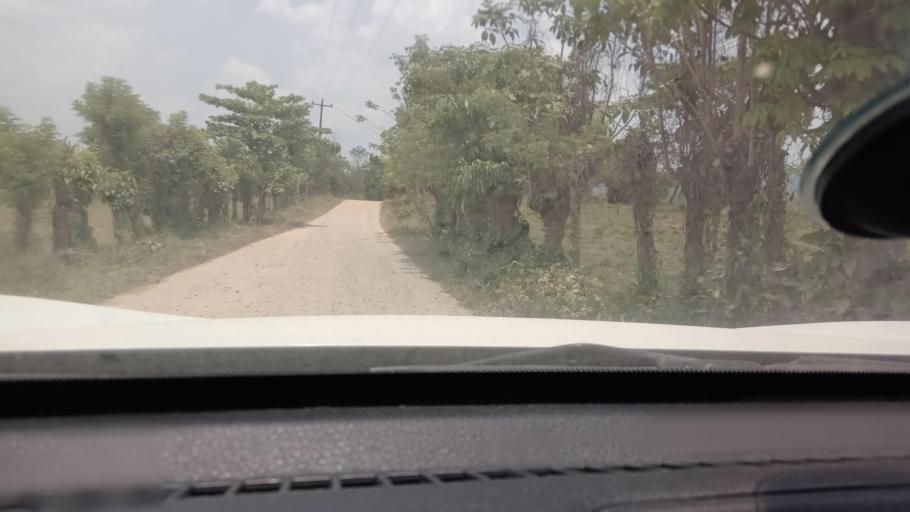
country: MX
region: Tabasco
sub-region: Huimanguillo
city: Francisco Rueda
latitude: 17.5079
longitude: -93.8991
